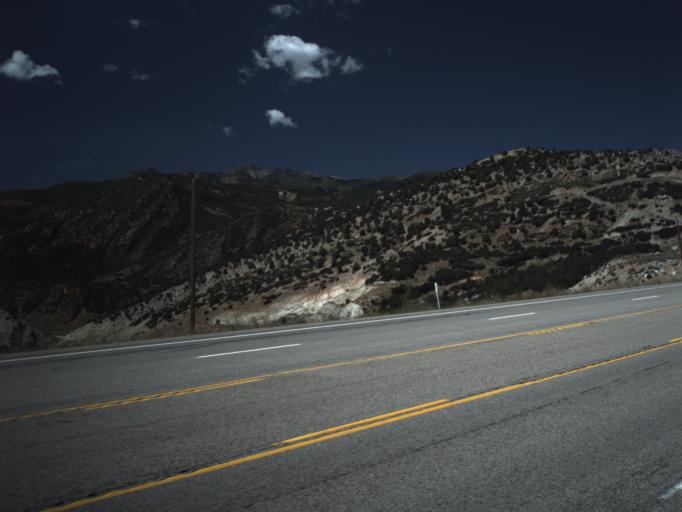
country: US
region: Utah
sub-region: Utah County
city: Mapleton
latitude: 39.9989
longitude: -111.4786
